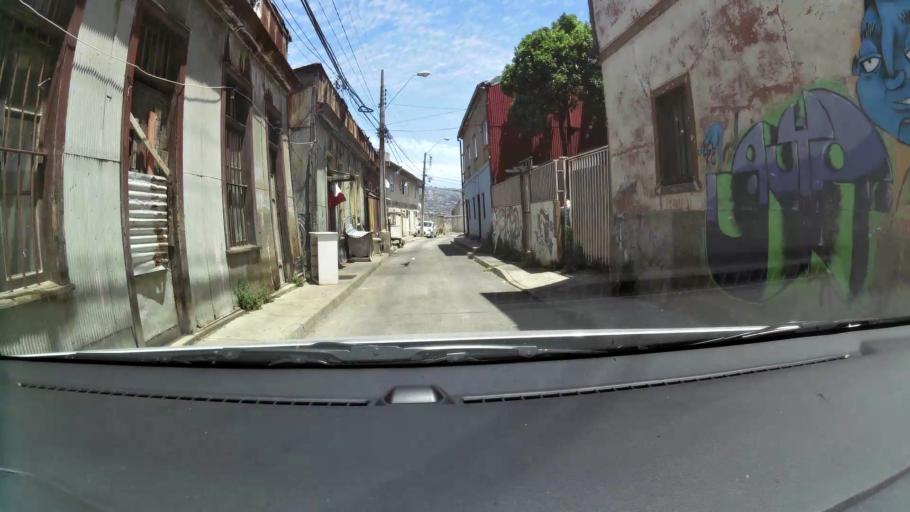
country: CL
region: Valparaiso
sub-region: Provincia de Valparaiso
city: Valparaiso
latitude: -33.0448
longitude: -71.6016
